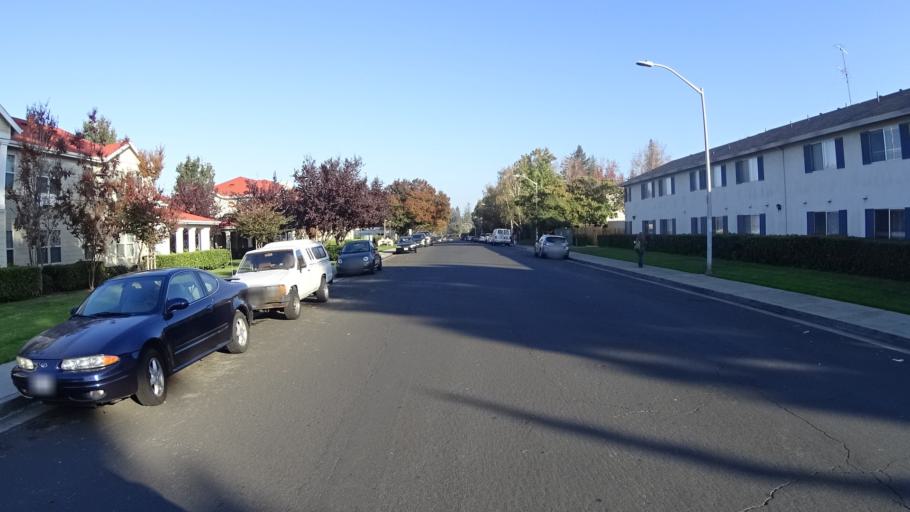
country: US
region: California
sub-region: Santa Clara County
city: Santa Clara
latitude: 37.3393
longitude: -121.9921
